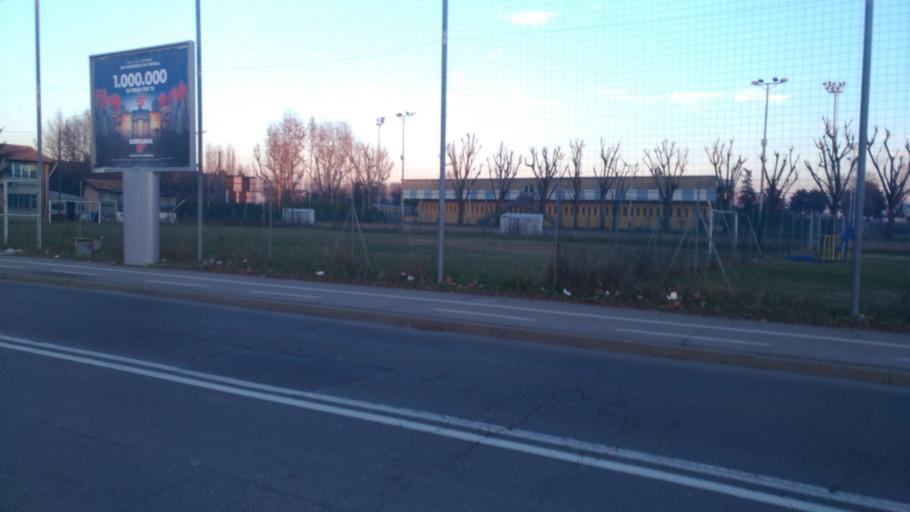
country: IT
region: Emilia-Romagna
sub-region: Provincia di Bologna
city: Bologna
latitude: 44.5270
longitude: 11.3460
